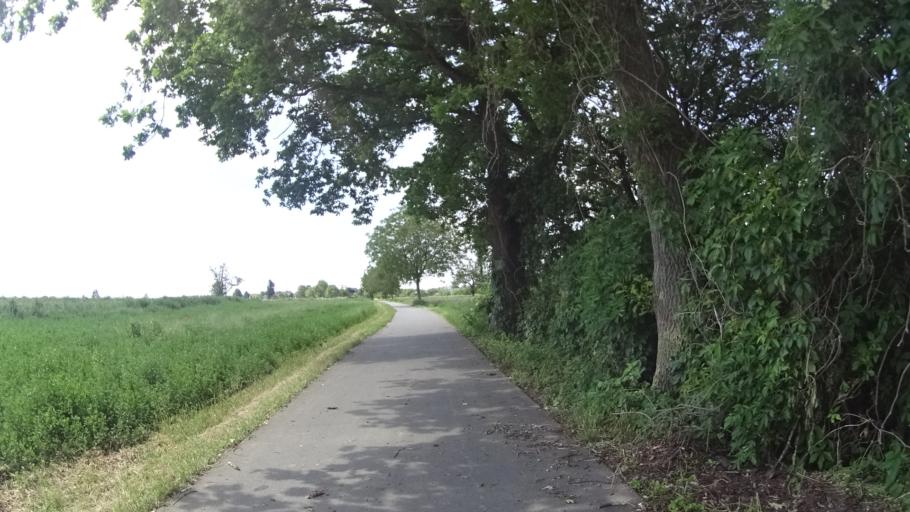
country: DE
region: Baden-Wuerttemberg
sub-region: Freiburg Region
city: Meissenheim
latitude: 48.3943
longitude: 7.7645
